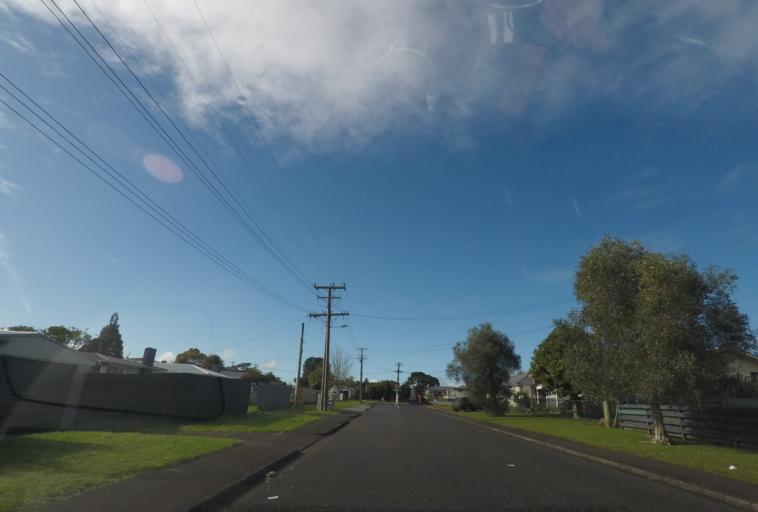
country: NZ
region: Auckland
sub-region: Auckland
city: Waitakere
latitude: -36.9008
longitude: 174.6623
